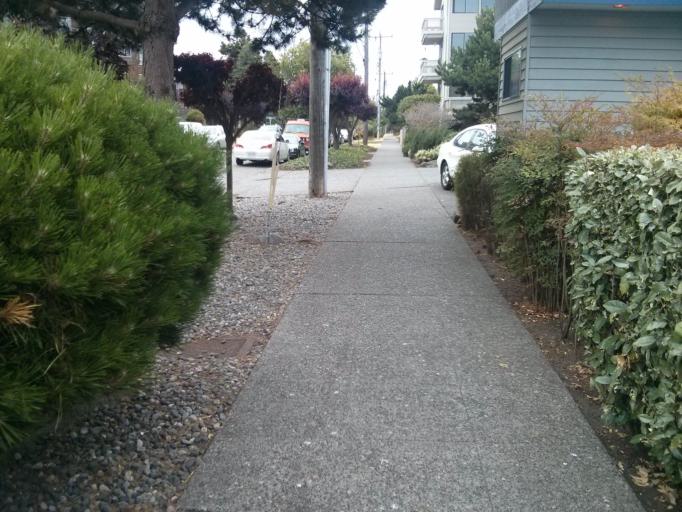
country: US
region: Washington
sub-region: King County
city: White Center
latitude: 47.5785
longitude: -122.4122
